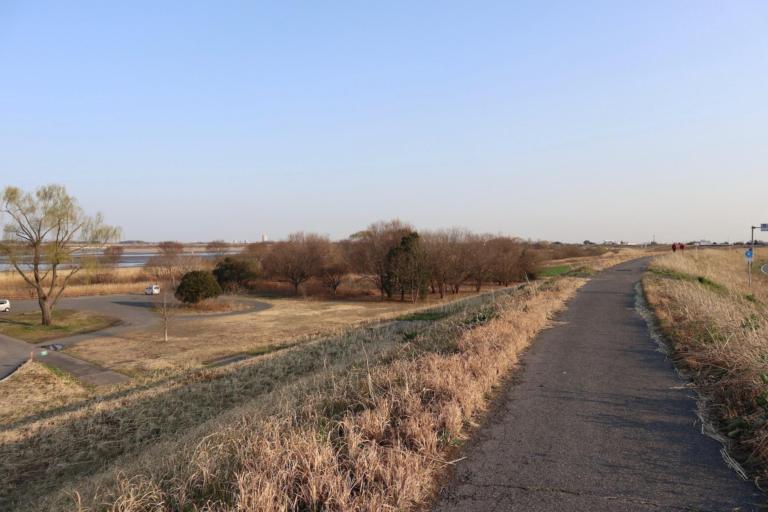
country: JP
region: Tochigi
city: Fujioka
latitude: 36.2242
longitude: 139.6567
